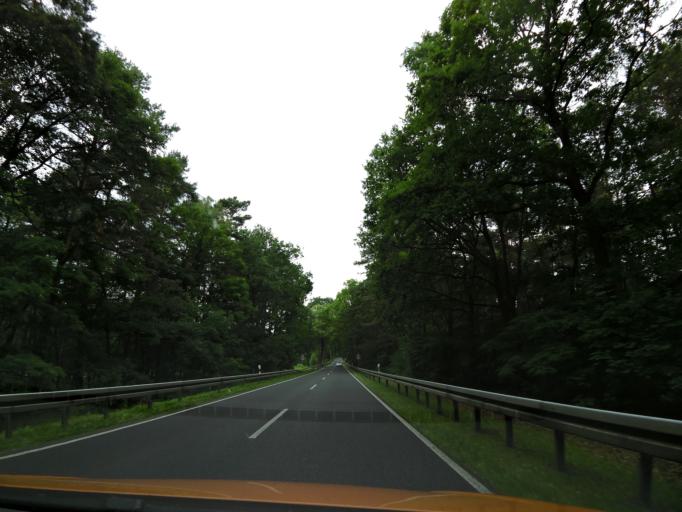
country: DE
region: Brandenburg
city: Baruth
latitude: 52.1175
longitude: 13.4856
